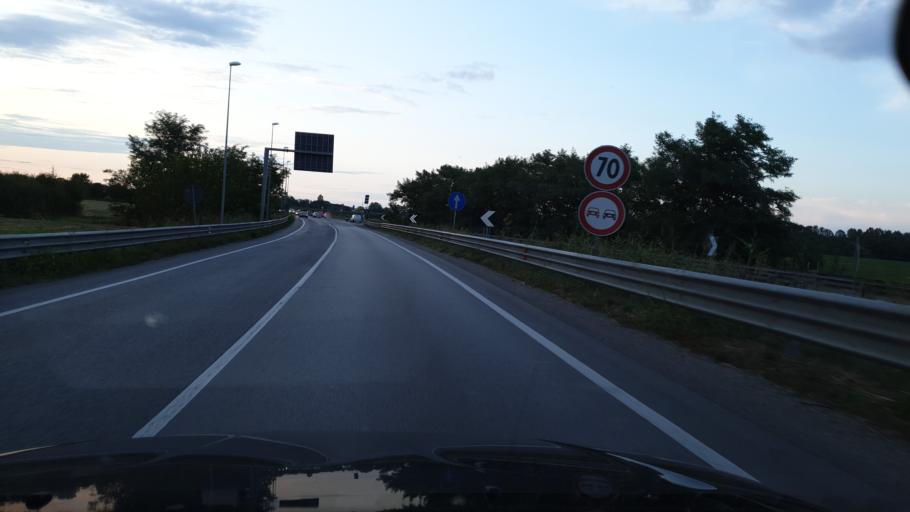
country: IT
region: Emilia-Romagna
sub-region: Provincia di Ravenna
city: Savio
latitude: 44.3195
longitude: 12.2837
